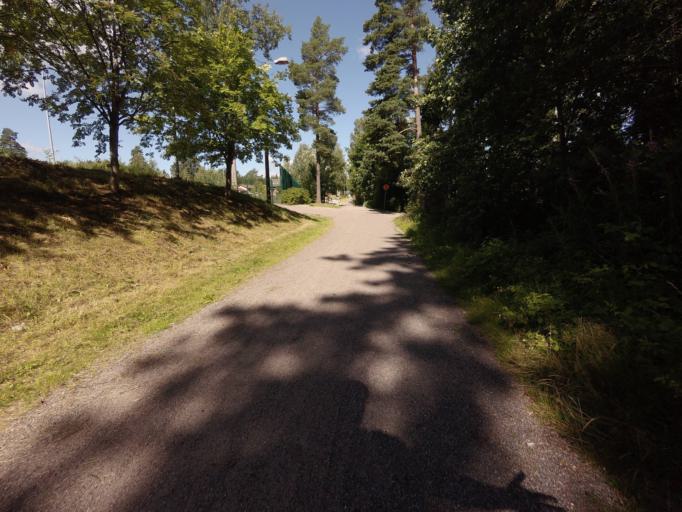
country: FI
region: Uusimaa
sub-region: Helsinki
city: Espoo
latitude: 60.1584
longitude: 24.6773
